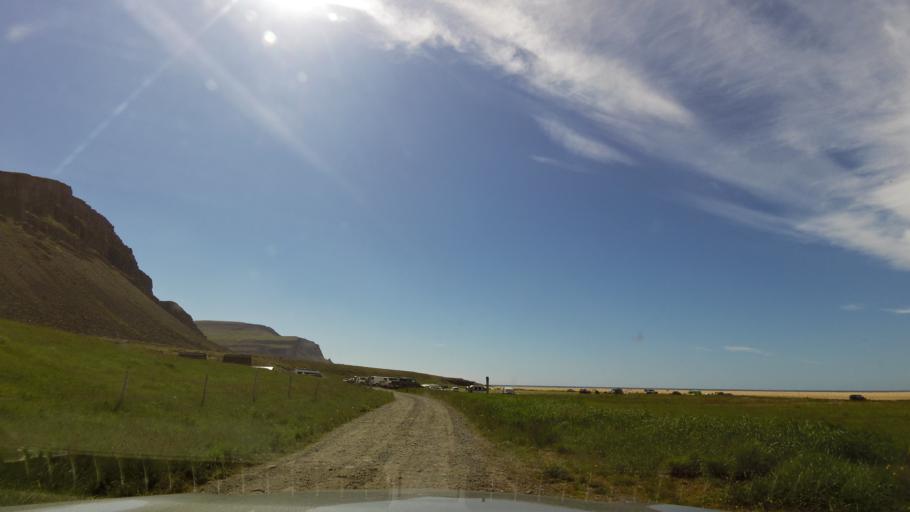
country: IS
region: West
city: Olafsvik
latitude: 65.4464
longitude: -23.9523
